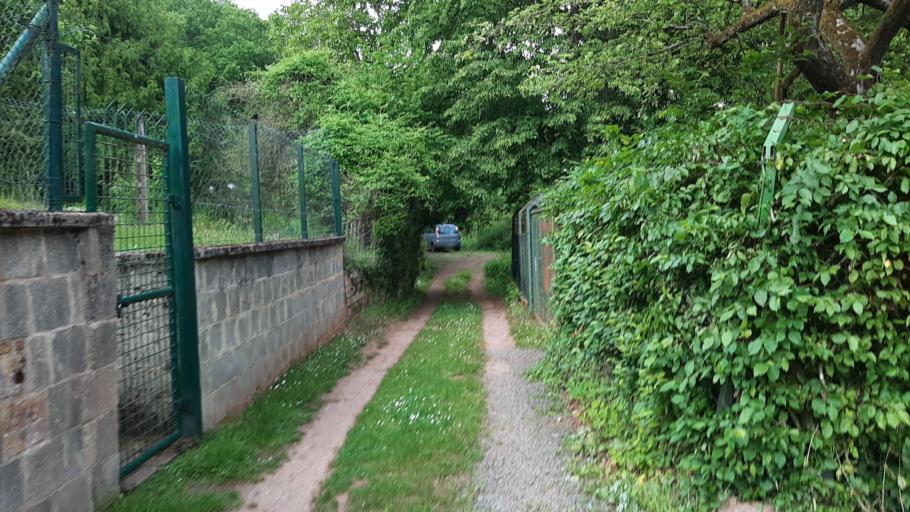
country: DE
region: Rheinland-Pfalz
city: Trier
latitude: 49.7425
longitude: 6.6057
